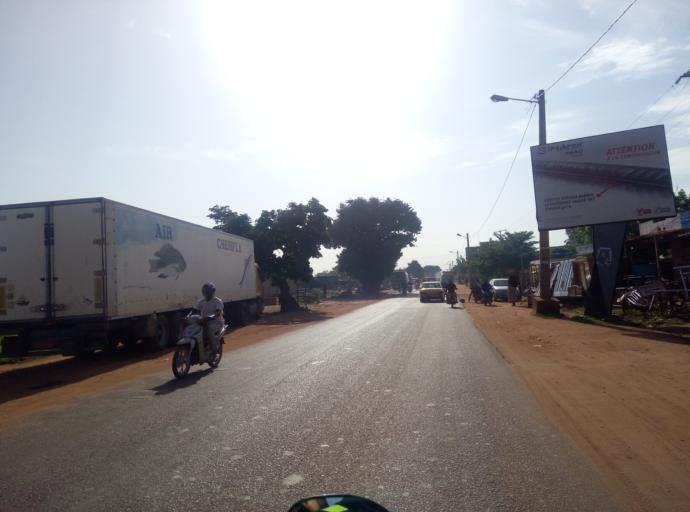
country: ML
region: Bamako
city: Bamako
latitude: 12.6522
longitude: -7.9462
